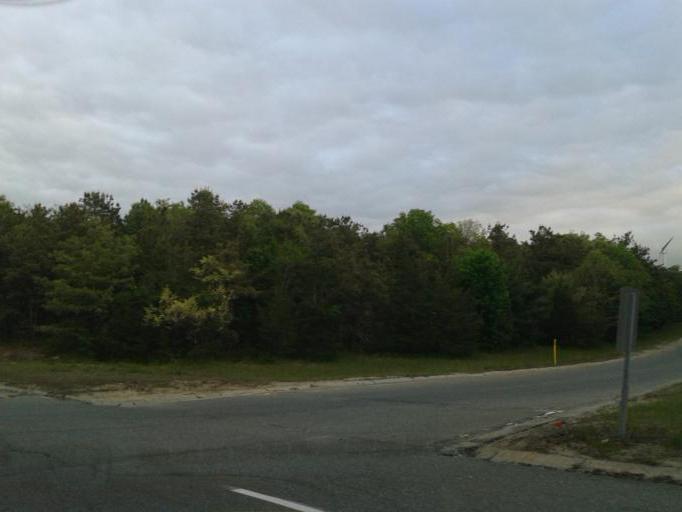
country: US
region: Massachusetts
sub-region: Barnstable County
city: West Falmouth
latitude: 41.6172
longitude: -70.6213
